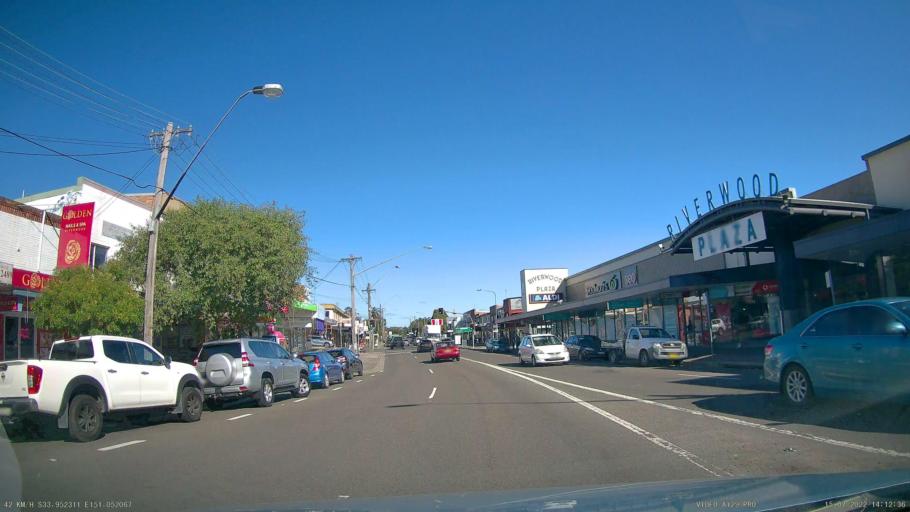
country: AU
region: New South Wales
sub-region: Hurstville
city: Peakhurst
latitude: -33.9523
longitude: 151.0520
